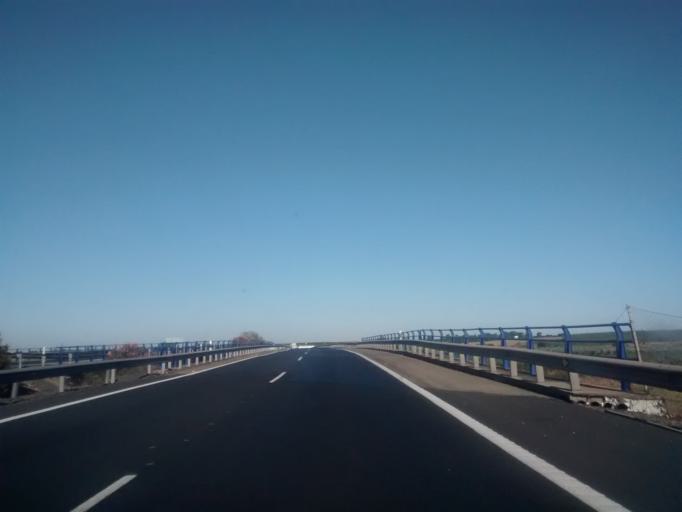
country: ES
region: Andalusia
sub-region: Provincia de Huelva
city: Lucena del Puerto
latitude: 37.3410
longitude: -6.7200
